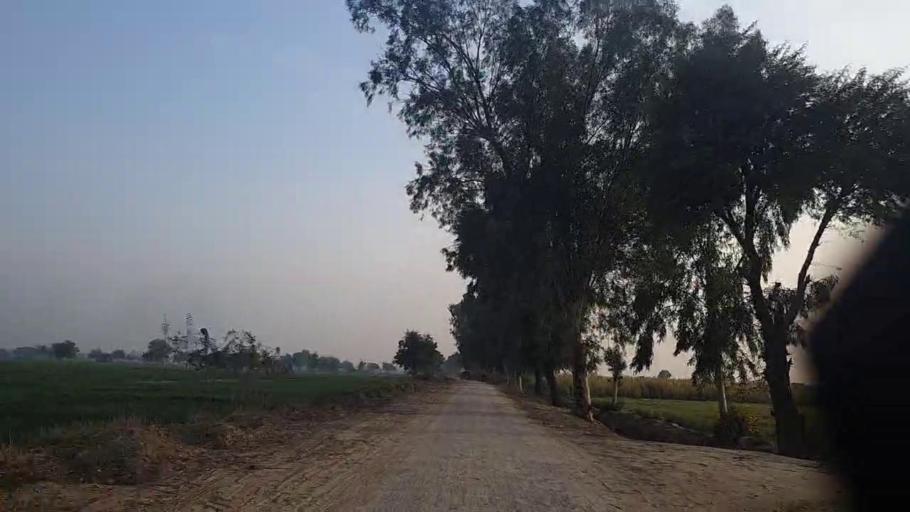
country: PK
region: Sindh
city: Sakrand
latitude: 26.1277
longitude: 68.2295
